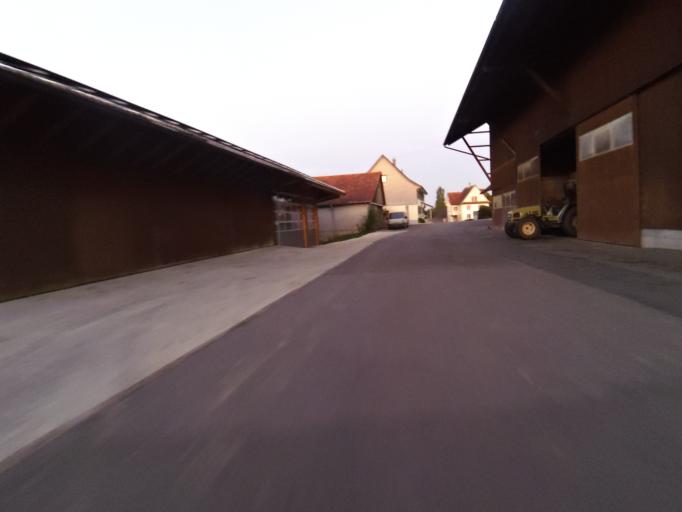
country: CH
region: Thurgau
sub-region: Weinfelden District
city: Wigoltingen
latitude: 47.5722
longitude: 9.0316
